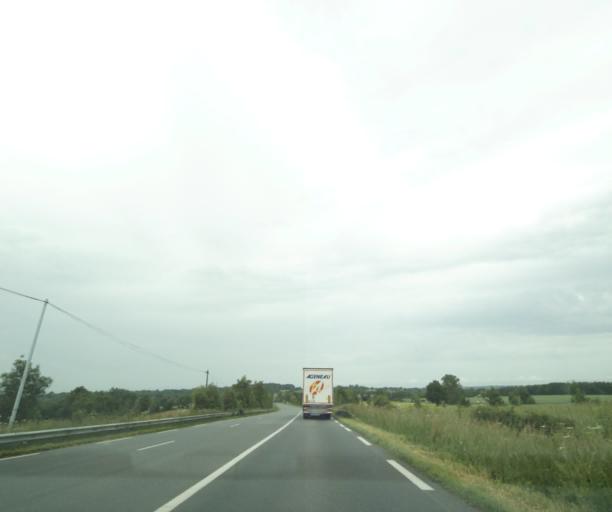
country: FR
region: Poitou-Charentes
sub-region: Departement des Deux-Sevres
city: Saint-Pardoux
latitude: 46.5790
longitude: -0.2930
